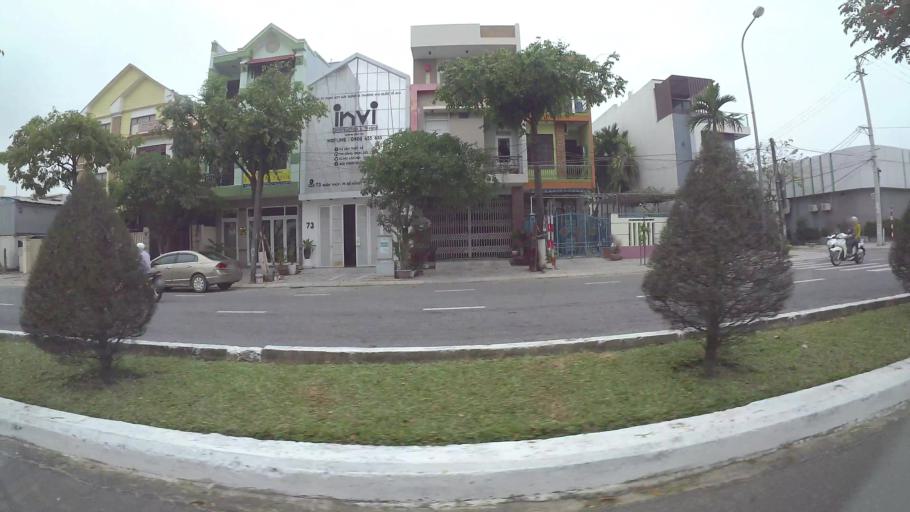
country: VN
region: Da Nang
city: Cam Le
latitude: 16.0267
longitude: 108.2145
